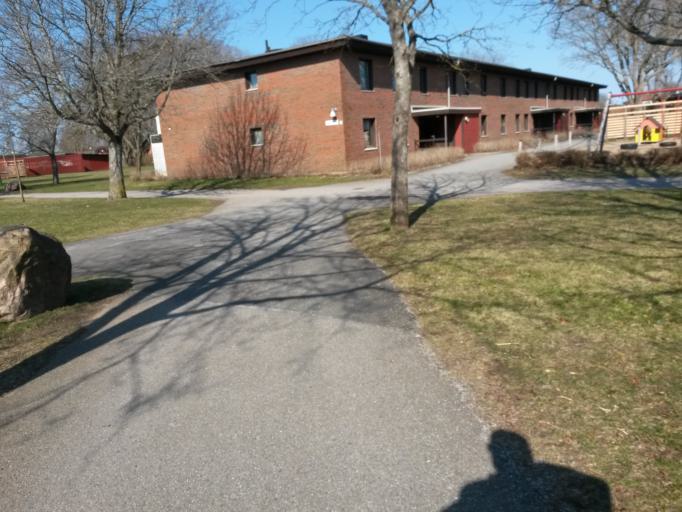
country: SE
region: Vaestra Goetaland
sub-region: Vargarda Kommun
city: Vargarda
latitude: 58.0354
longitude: 12.8045
